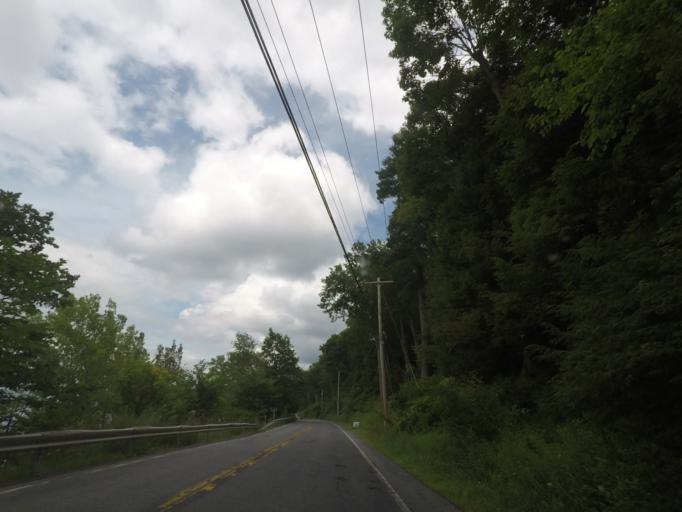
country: US
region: New York
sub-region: Saratoga County
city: Stillwater
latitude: 42.9937
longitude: -73.7364
